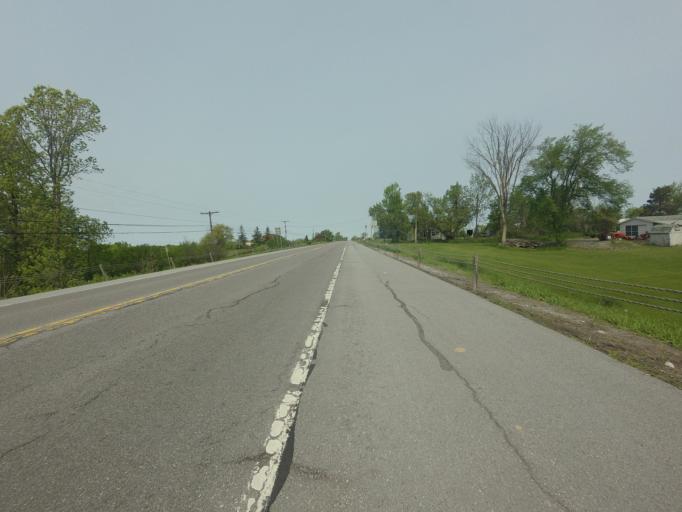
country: US
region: New York
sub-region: Jefferson County
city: Dexter
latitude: 44.0299
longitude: -76.0493
